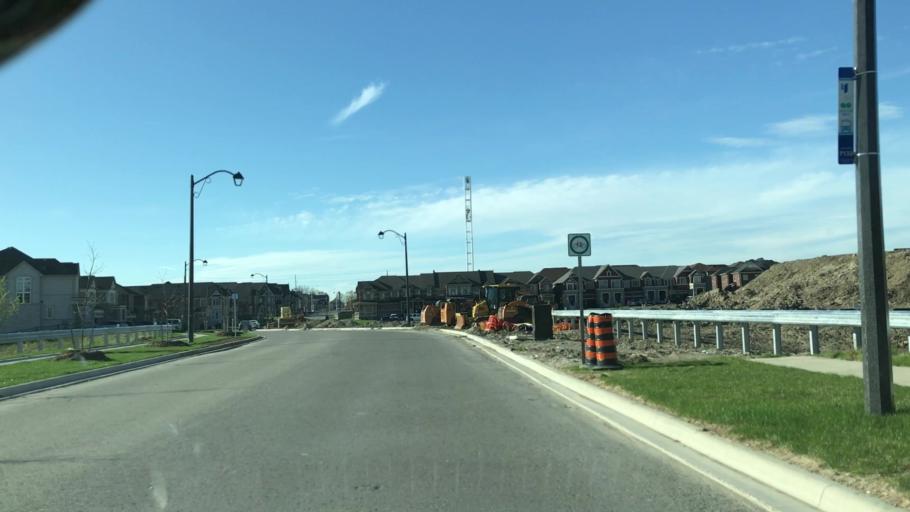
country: CA
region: Ontario
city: Newmarket
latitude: 44.0235
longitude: -79.4290
